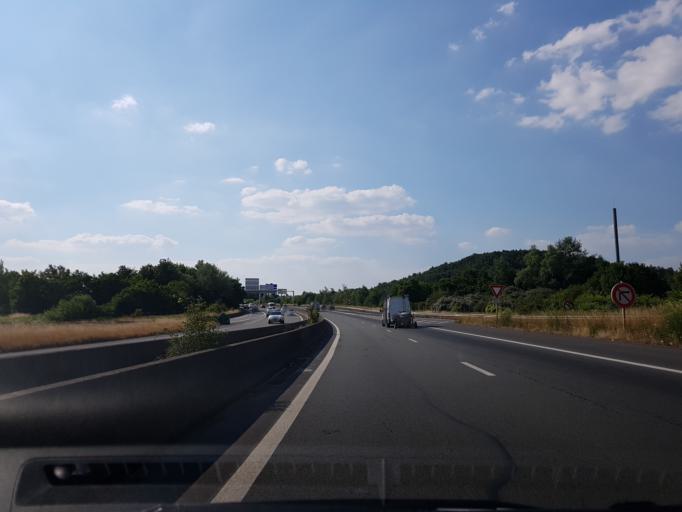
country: FR
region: Nord-Pas-de-Calais
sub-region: Departement du Nord
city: Waziers
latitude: 50.3974
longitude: 3.1154
